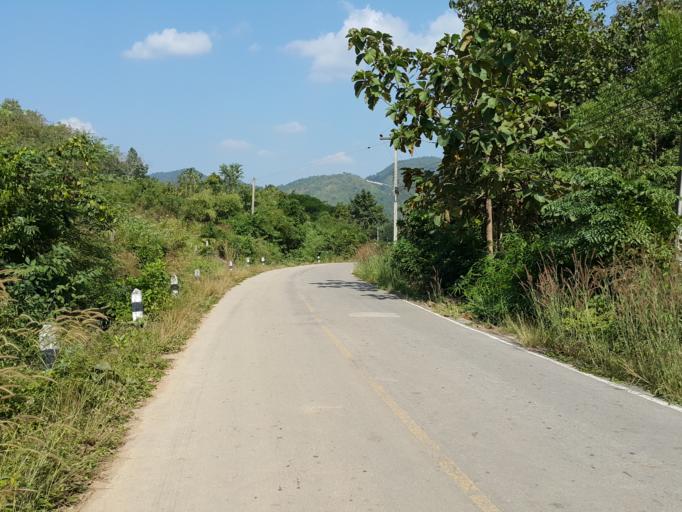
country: TH
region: Sukhothai
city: Thung Saliam
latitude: 17.3356
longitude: 99.4585
